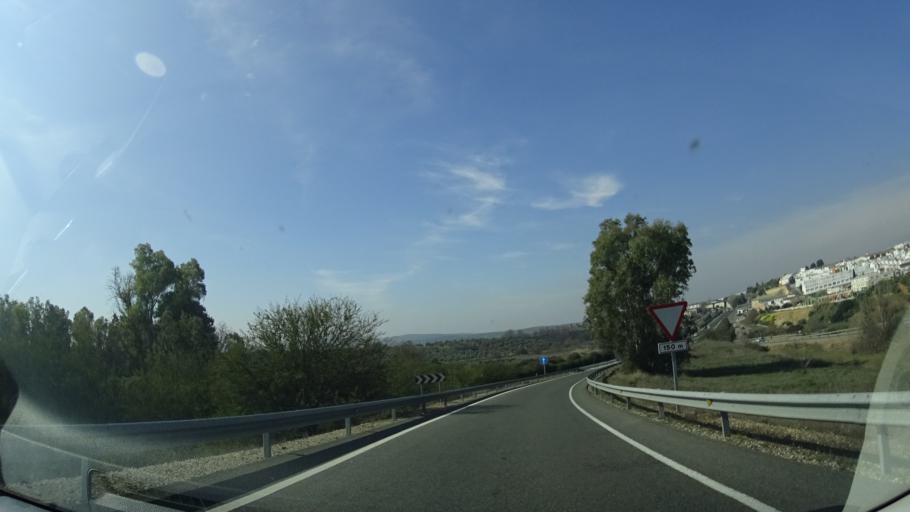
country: ES
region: Andalusia
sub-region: Province of Cordoba
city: Montoro
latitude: 38.0111
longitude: -4.3722
